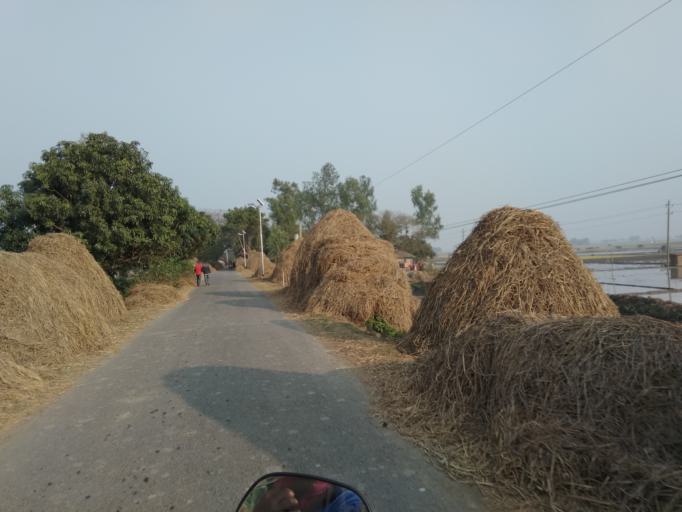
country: BD
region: Rajshahi
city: Par Naogaon
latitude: 24.4989
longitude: 89.1531
